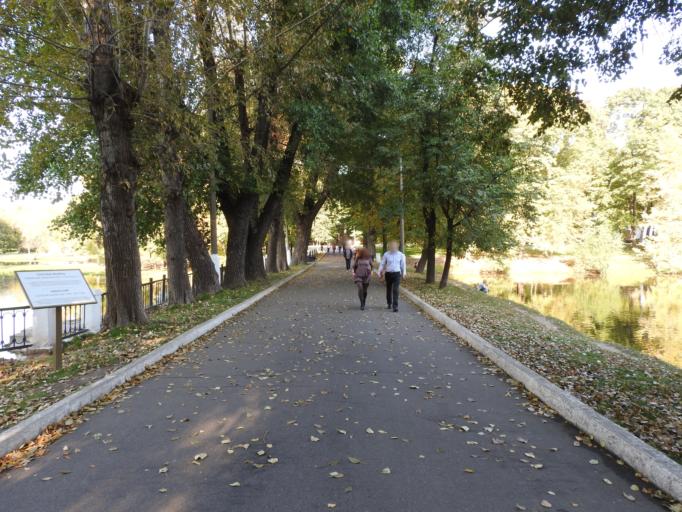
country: RU
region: Moscow
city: Lefortovo
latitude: 55.7629
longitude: 37.6890
